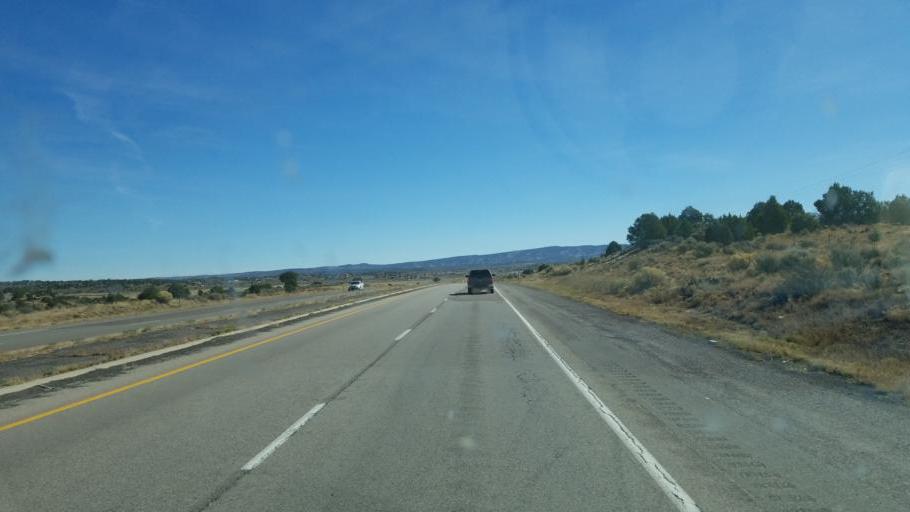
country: US
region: New Mexico
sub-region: McKinley County
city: Twin Lakes
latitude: 35.6360
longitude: -108.8361
